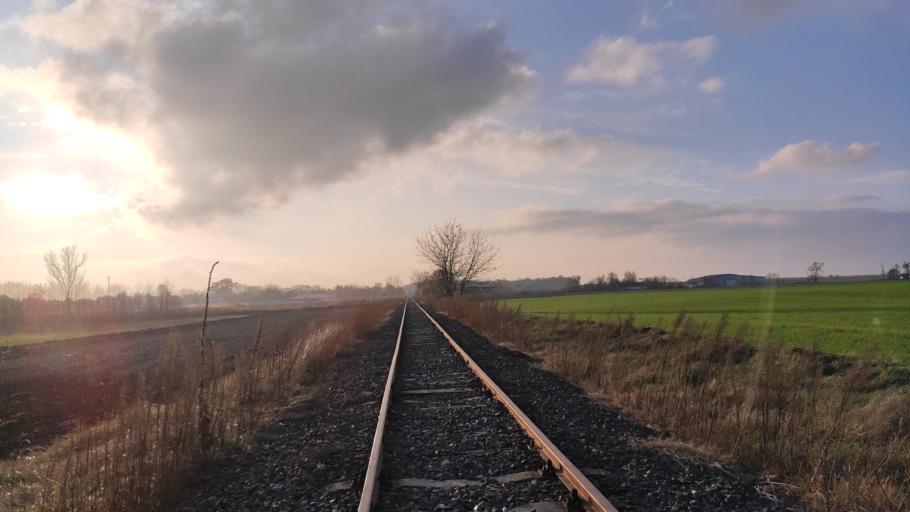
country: HU
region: Bekes
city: Mezobereny
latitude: 46.7653
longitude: 21.0504
